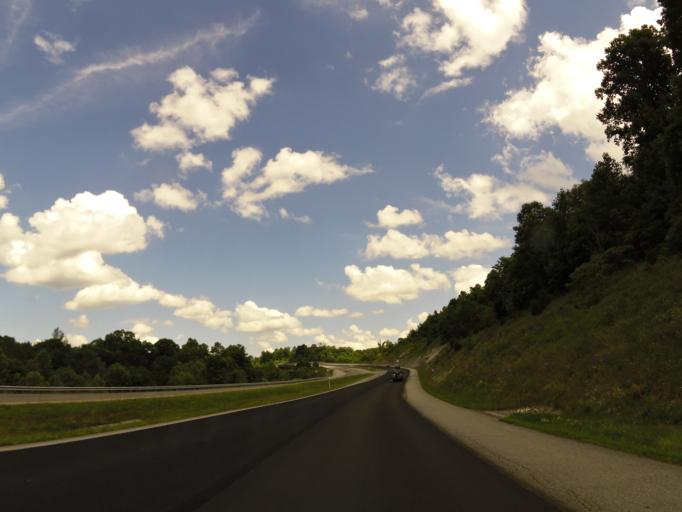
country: US
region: Kentucky
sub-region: Harlan County
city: Harlan
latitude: 36.6921
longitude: -83.2926
